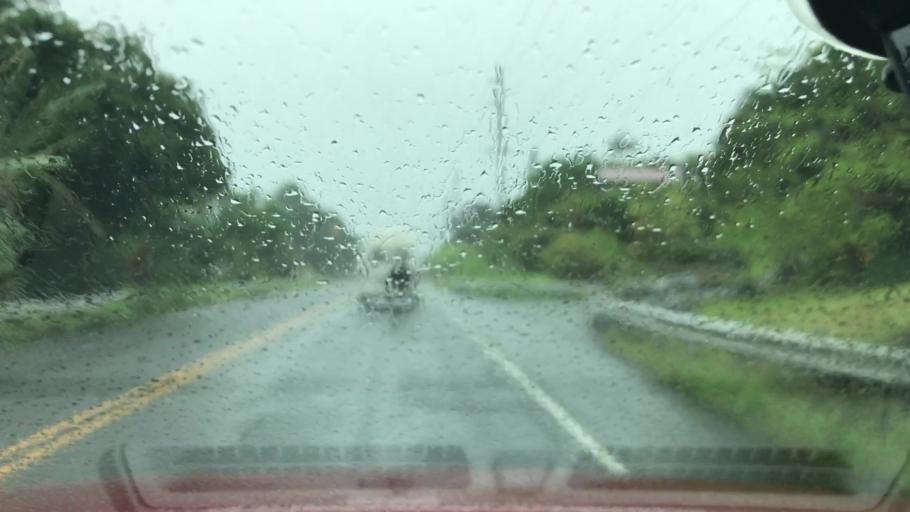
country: US
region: Hawaii
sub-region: Hawaii County
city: Pepeekeo
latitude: 19.9856
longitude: -155.2390
